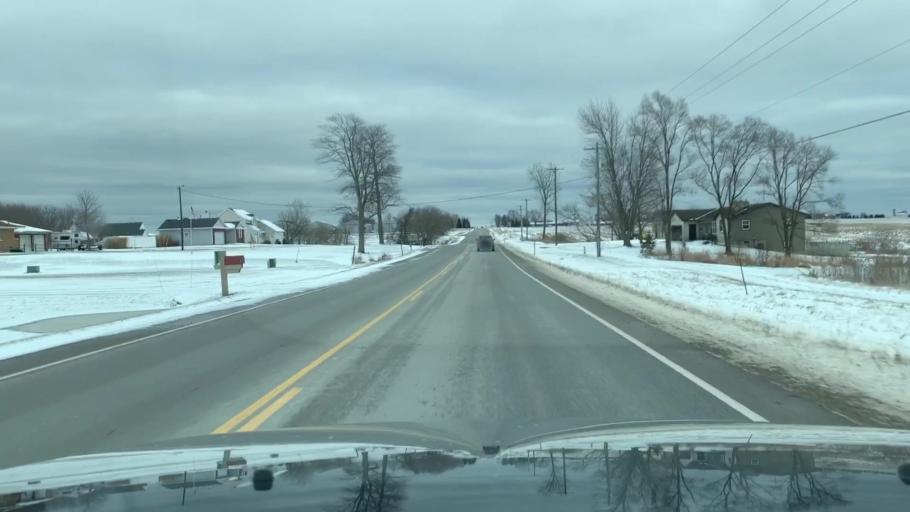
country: US
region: Michigan
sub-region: Ottawa County
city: Zeeland
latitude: 42.8115
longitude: -85.9340
